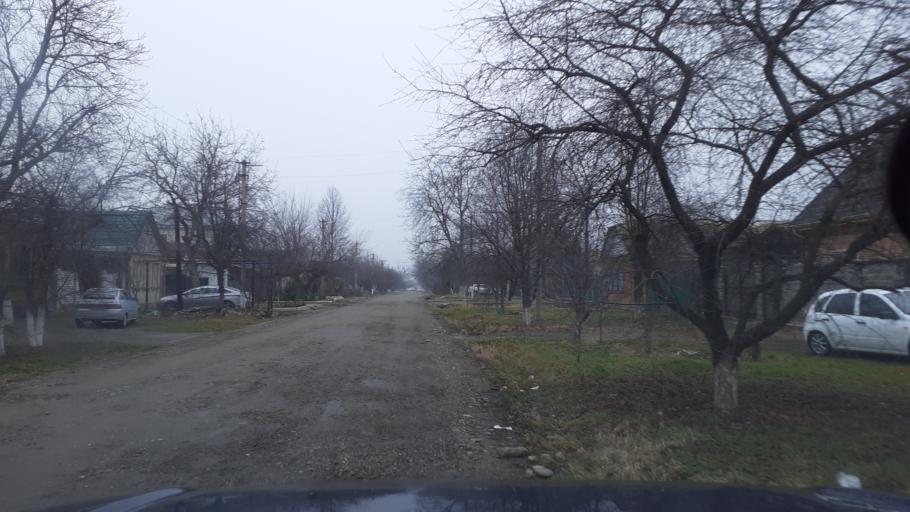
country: RU
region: Adygeya
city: Maykop
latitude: 44.6146
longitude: 40.0874
